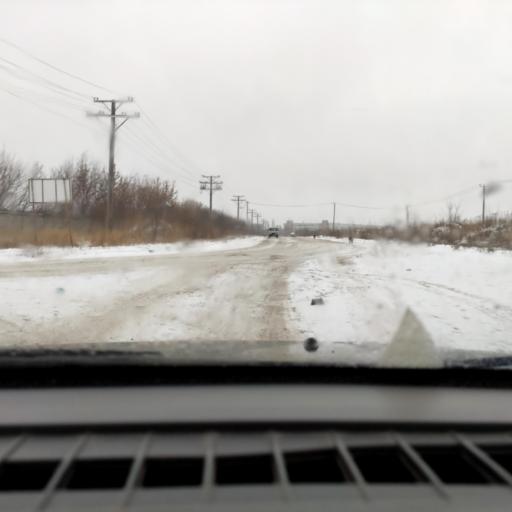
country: RU
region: Samara
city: Tol'yatti
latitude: 53.5537
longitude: 49.3284
